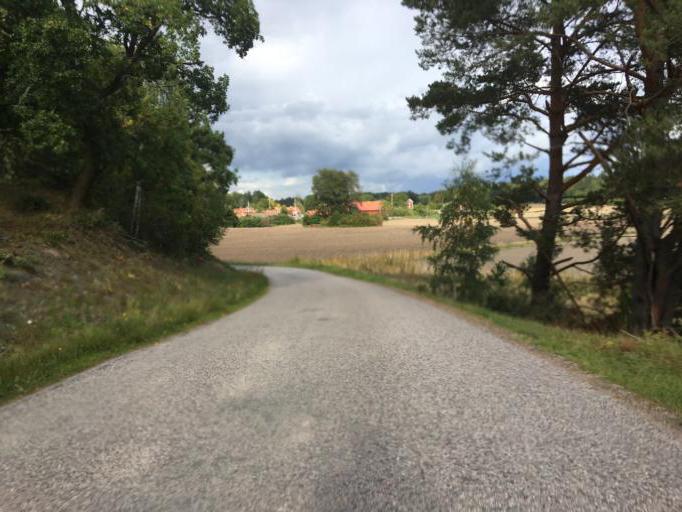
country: SE
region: Soedermanland
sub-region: Eskilstuna Kommun
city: Eskilstuna
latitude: 59.4451
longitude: 16.6411
